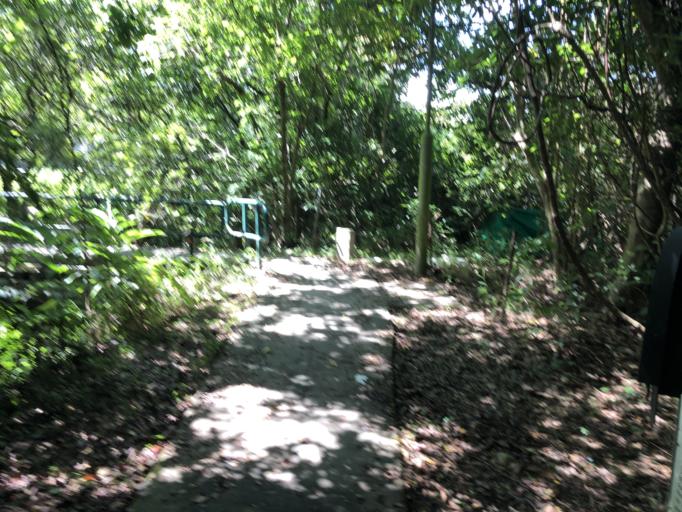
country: HK
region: Tuen Mun
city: Tuen Mun
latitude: 22.2892
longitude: 113.9790
